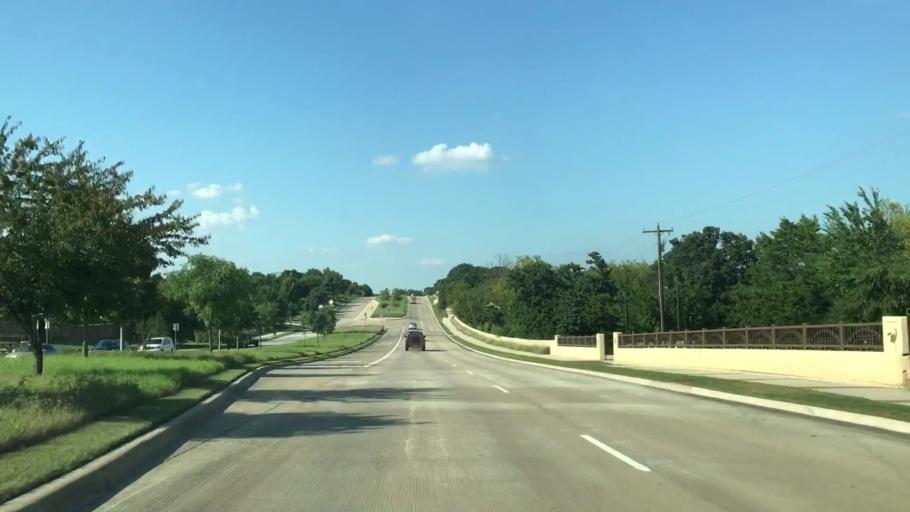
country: US
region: Texas
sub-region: Denton County
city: Trophy Club
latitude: 32.9634
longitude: -97.1858
